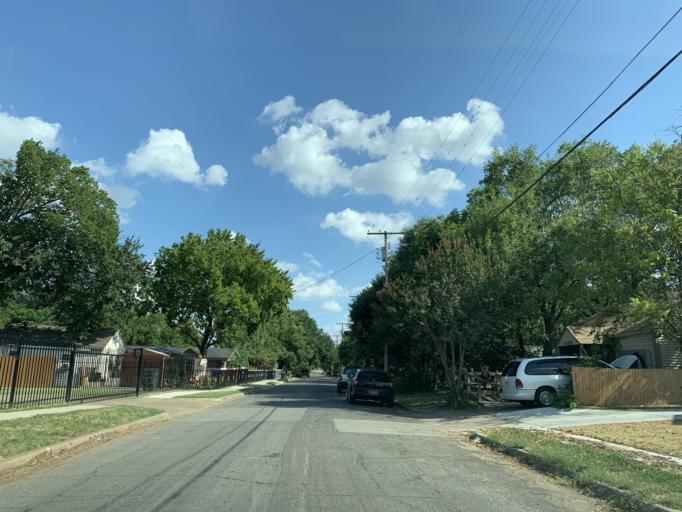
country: US
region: Texas
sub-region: Dallas County
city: Dallas
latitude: 32.7034
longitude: -96.7822
